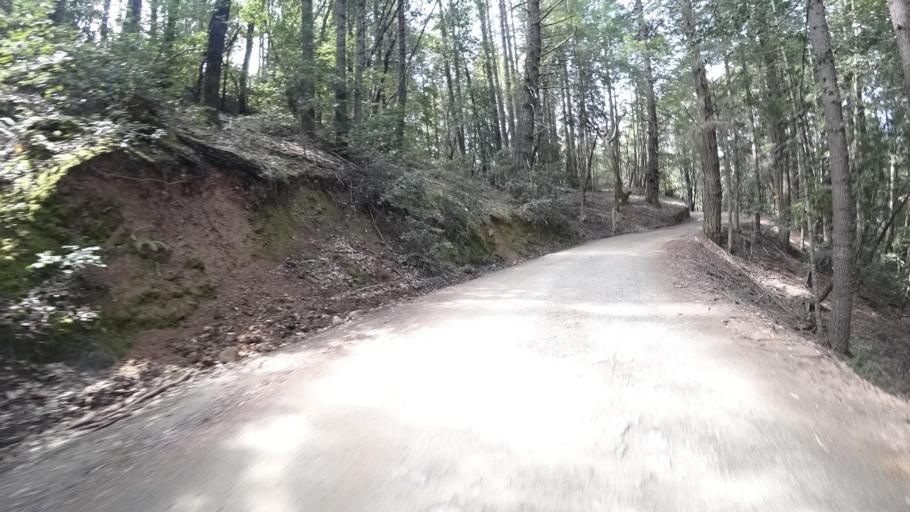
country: US
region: California
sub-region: Humboldt County
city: Redway
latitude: 40.0276
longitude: -123.8421
